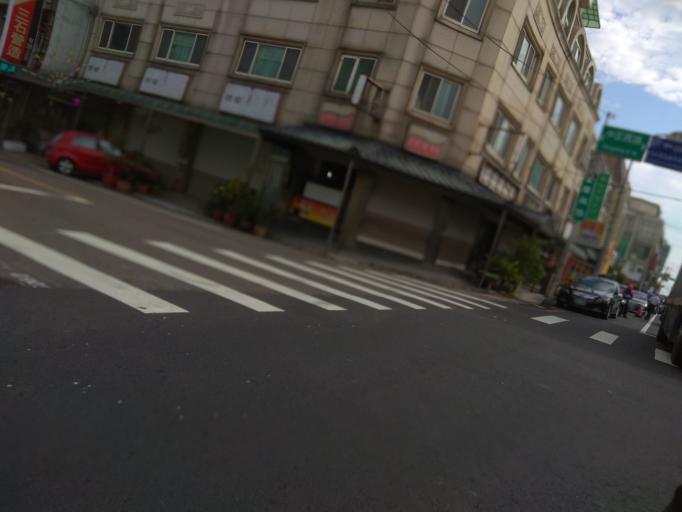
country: TW
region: Taiwan
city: Taoyuan City
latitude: 25.0632
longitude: 121.1937
